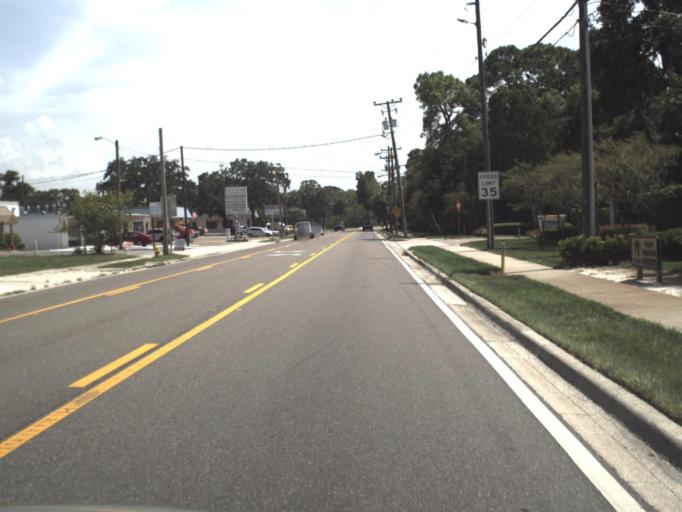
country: US
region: Florida
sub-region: Pinellas County
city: Dunedin
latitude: 28.0233
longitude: -82.7897
